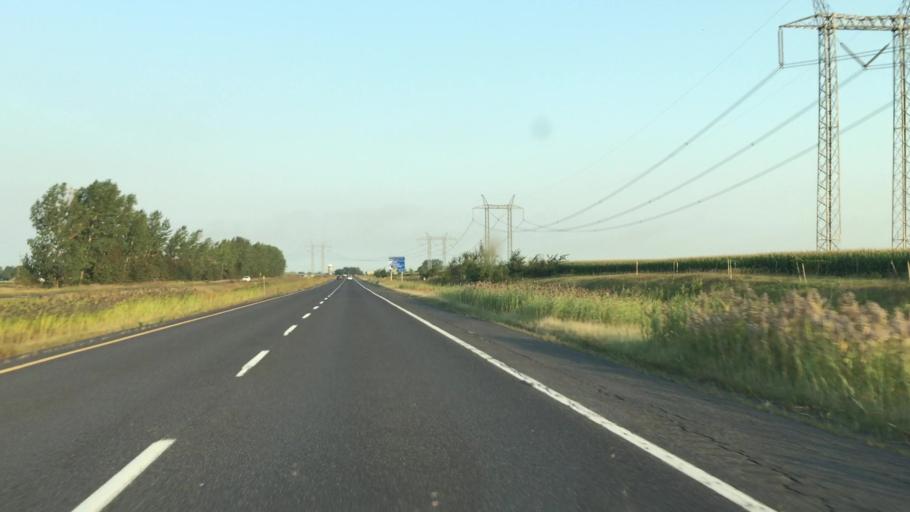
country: CA
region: Quebec
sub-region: Monteregie
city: Marieville
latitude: 45.4112
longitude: -73.2067
